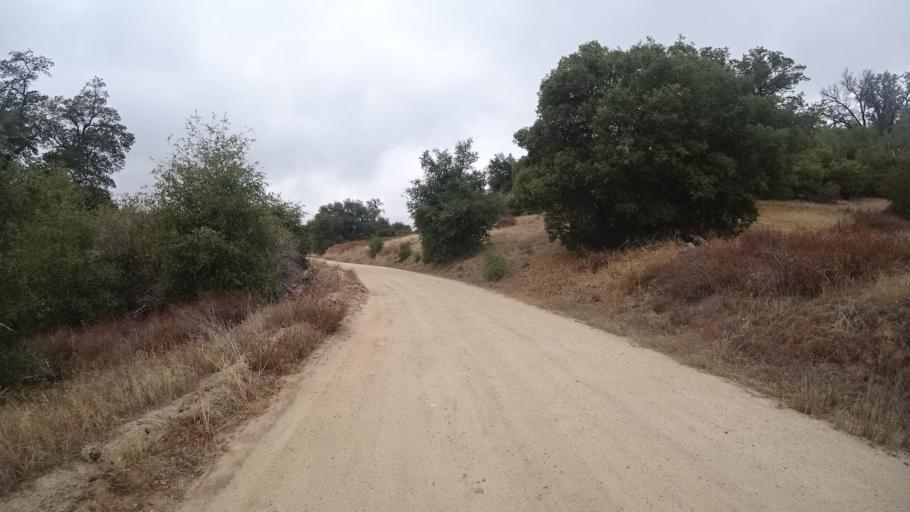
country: US
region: California
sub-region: San Diego County
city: Julian
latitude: 33.0149
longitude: -116.6316
